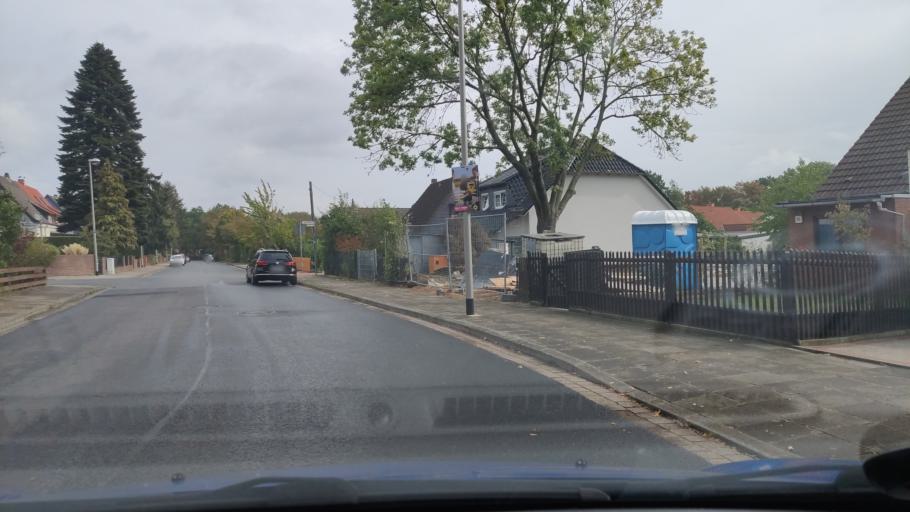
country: DE
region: Lower Saxony
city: Ronnenberg
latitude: 52.3700
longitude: 9.6669
